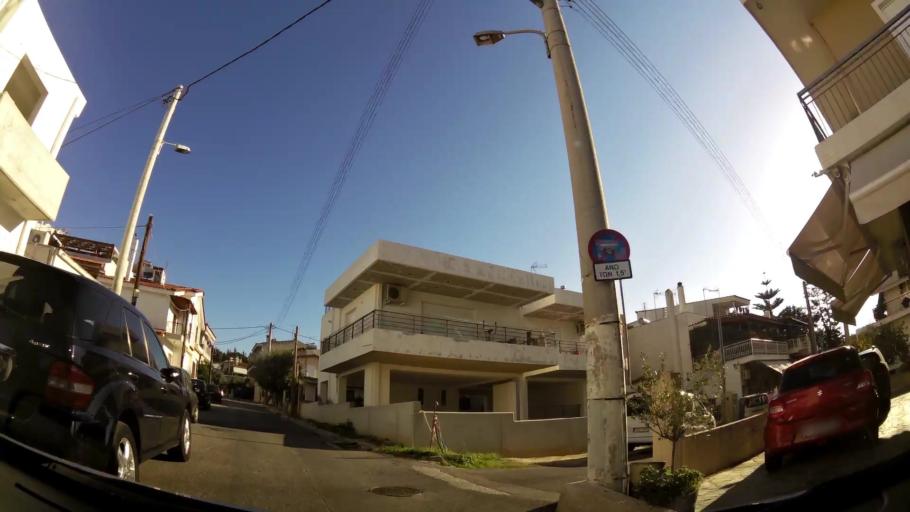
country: GR
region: Attica
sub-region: Nomarchia Athinas
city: Lykovrysi
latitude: 38.0554
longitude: 23.7808
